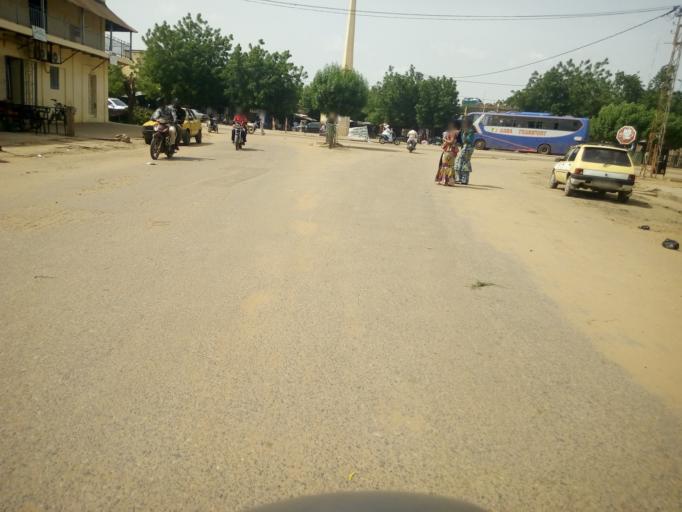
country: ML
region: Kayes
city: Kayes
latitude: 14.4455
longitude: -11.4386
